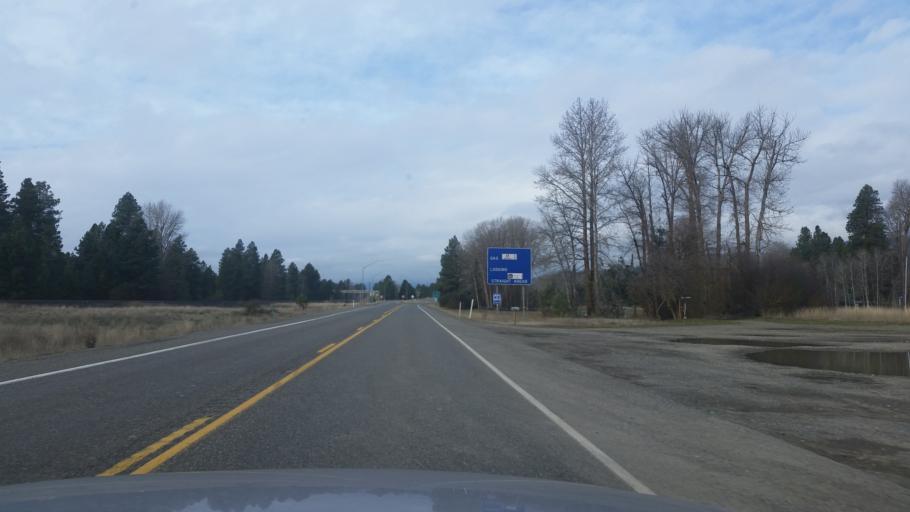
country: US
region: Washington
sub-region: Kittitas County
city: Cle Elum
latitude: 47.1851
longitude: -120.8920
